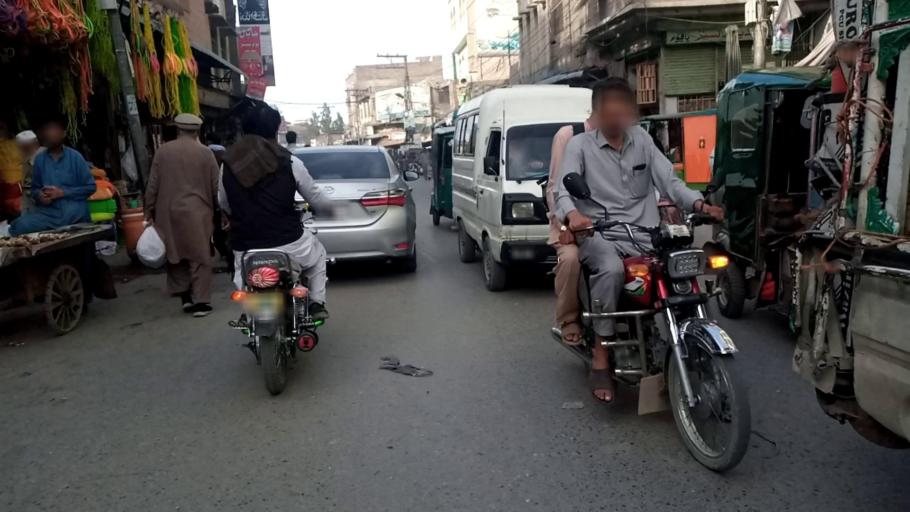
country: PK
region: Khyber Pakhtunkhwa
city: Peshawar
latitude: 34.0117
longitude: 71.5746
